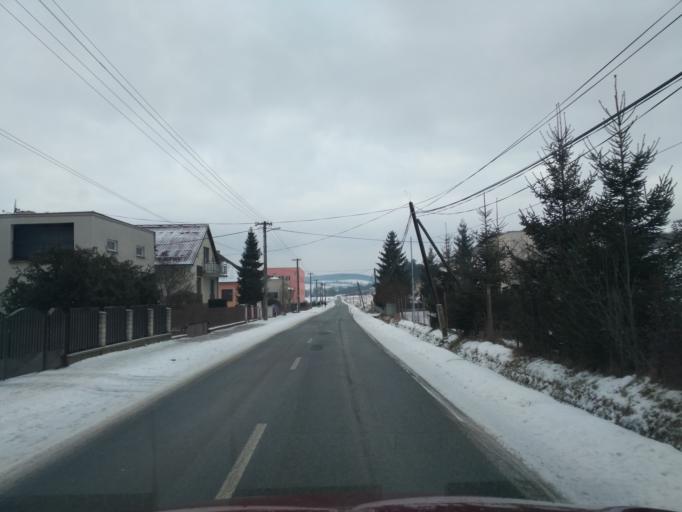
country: SK
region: Presovsky
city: Sabinov
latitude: 49.0152
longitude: 21.1192
